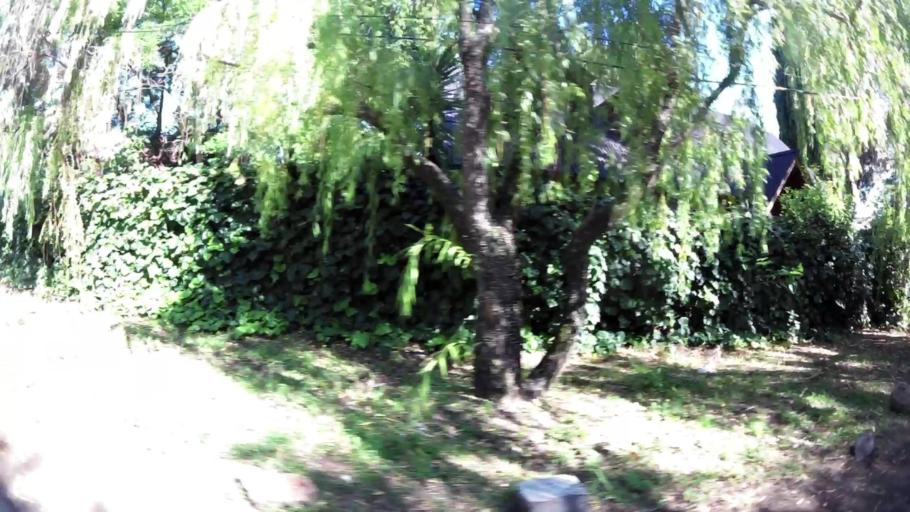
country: AR
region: Buenos Aires
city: Ituzaingo
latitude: -34.6295
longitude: -58.6555
